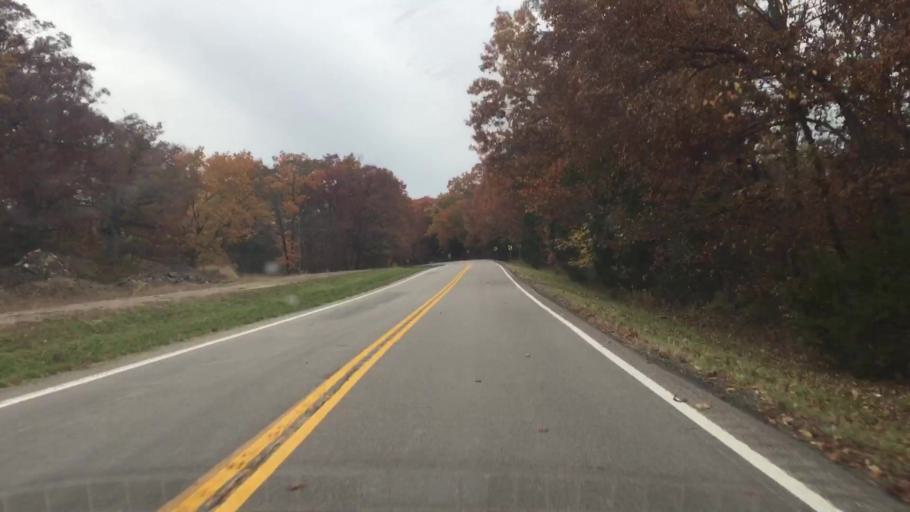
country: US
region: Missouri
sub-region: Gasconade County
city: Hermann
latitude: 38.7197
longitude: -91.6705
